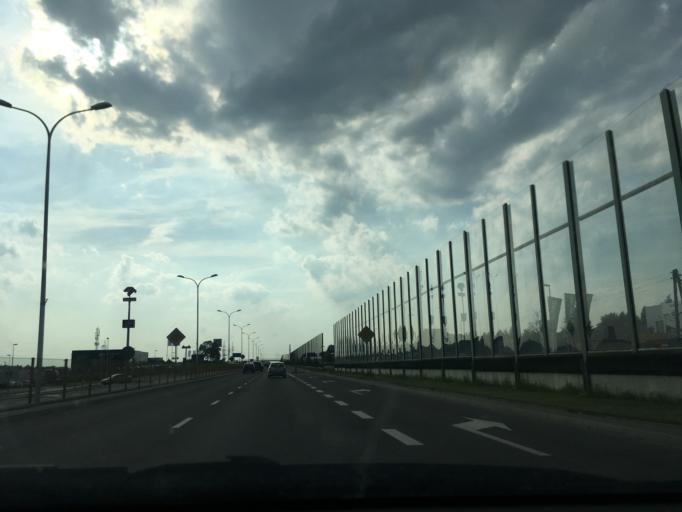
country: PL
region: Podlasie
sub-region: Bialystok
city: Bialystok
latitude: 53.1595
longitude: 23.1205
